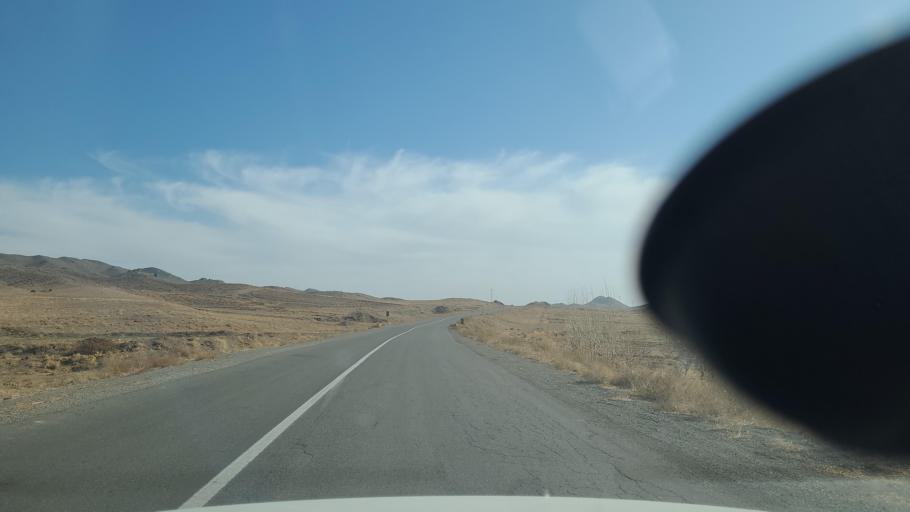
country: IR
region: Razavi Khorasan
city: Fariman
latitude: 35.5976
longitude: 59.7036
